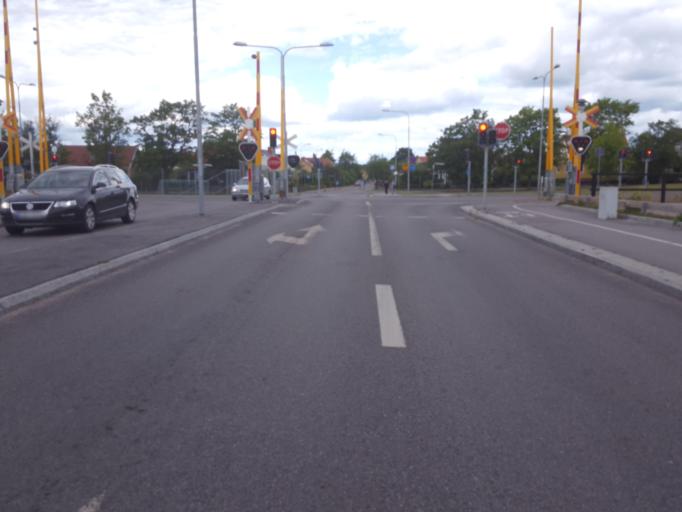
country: SE
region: Uppsala
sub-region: Uppsala Kommun
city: Uppsala
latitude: 59.8571
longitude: 17.6650
